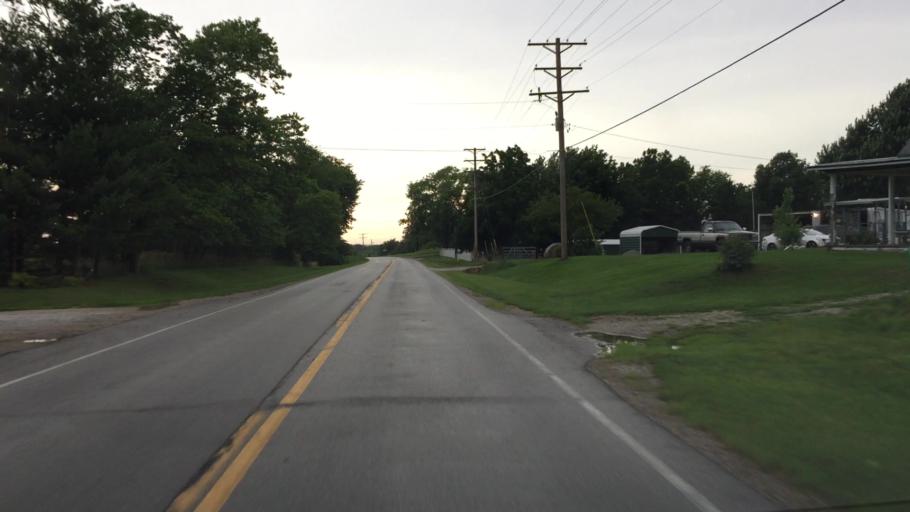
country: US
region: Illinois
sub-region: Hancock County
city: Warsaw
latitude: 40.3549
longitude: -91.4074
